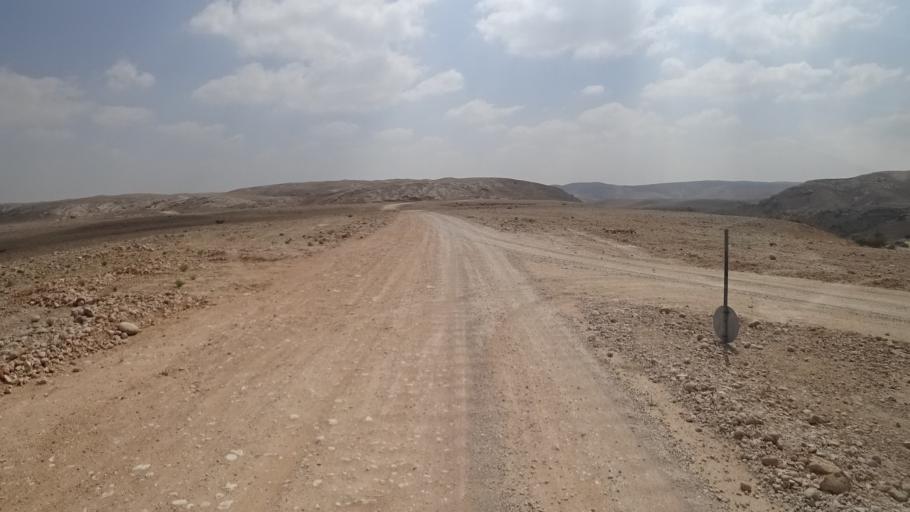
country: OM
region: Zufar
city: Salalah
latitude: 17.2396
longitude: 53.8947
